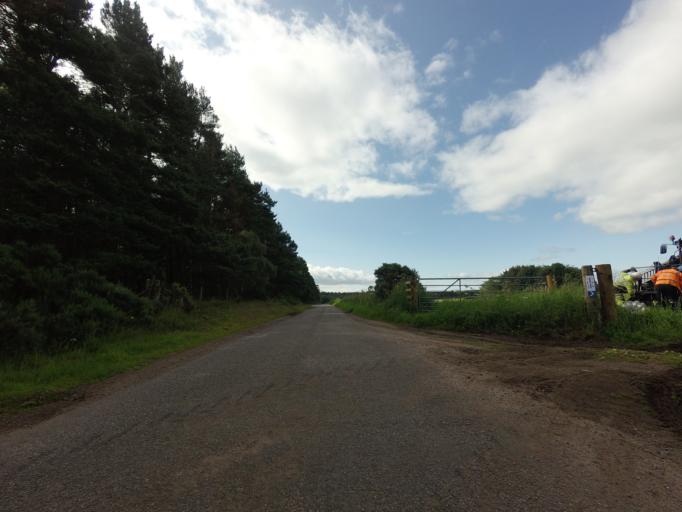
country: GB
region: Scotland
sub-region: Highland
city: Nairn
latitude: 57.5656
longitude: -3.8668
